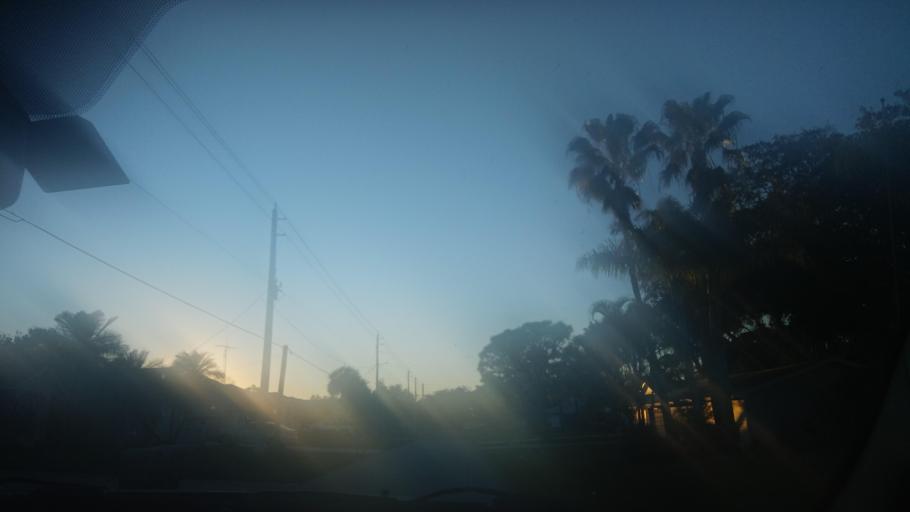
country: US
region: Florida
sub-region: Indian River County
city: Sebastian
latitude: 27.7567
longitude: -80.4928
